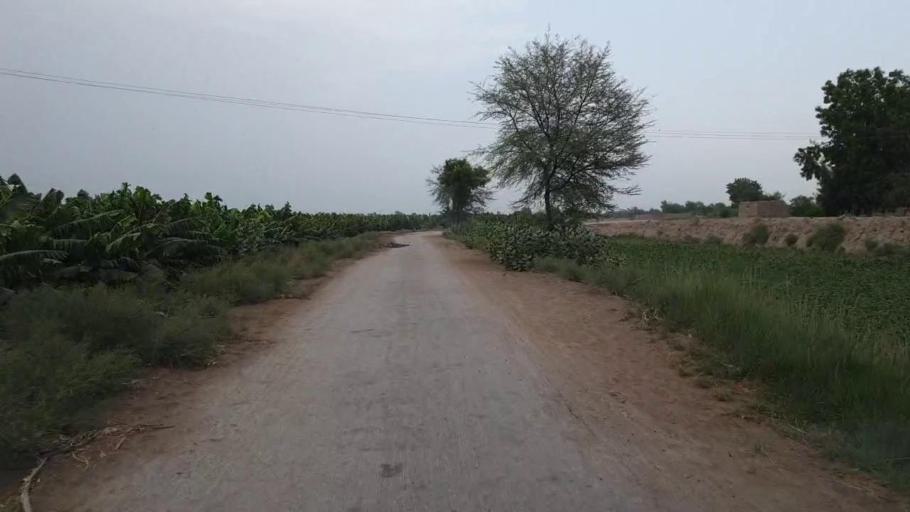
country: PK
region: Sindh
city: Bandhi
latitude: 26.5331
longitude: 68.2013
